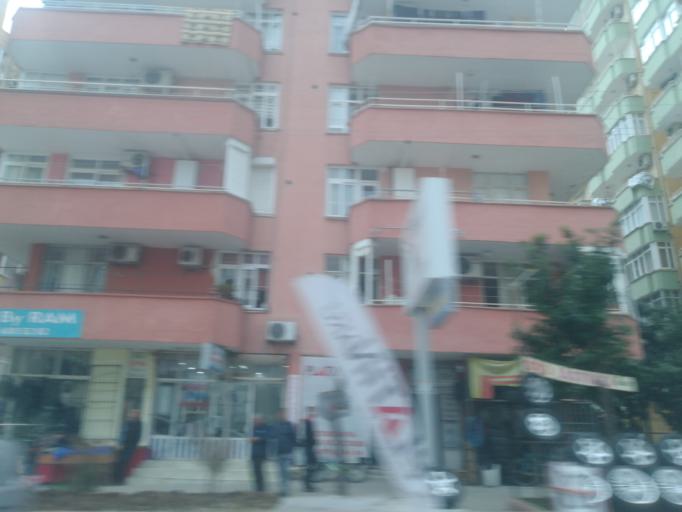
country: TR
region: Adana
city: Adana
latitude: 37.0455
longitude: 35.2902
